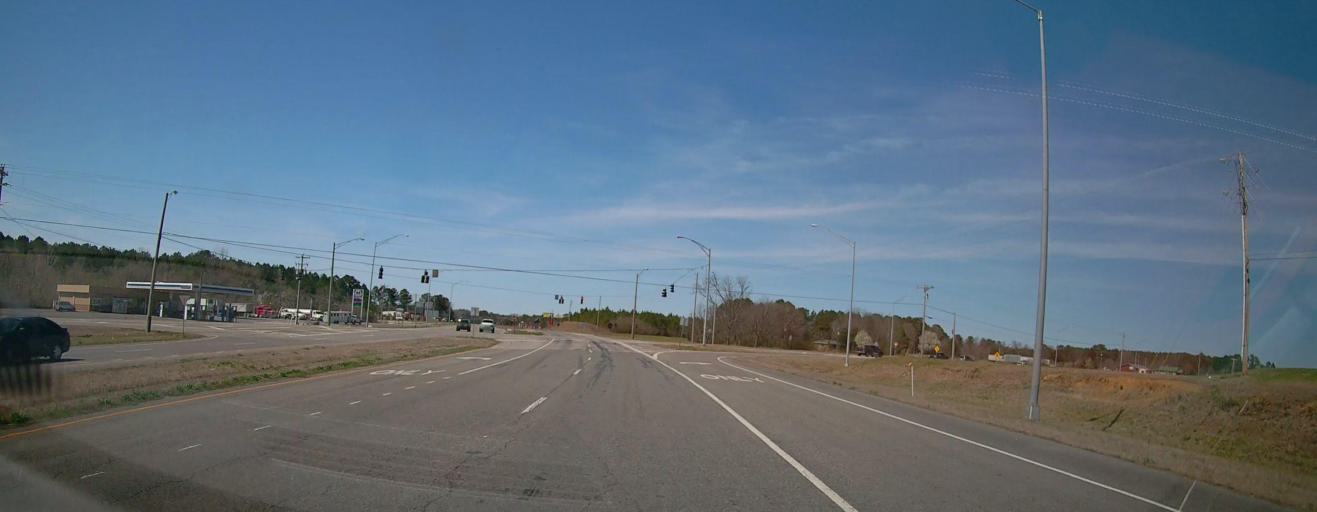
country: US
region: Alabama
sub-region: Cullman County
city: Cullman
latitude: 34.1916
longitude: -86.7856
